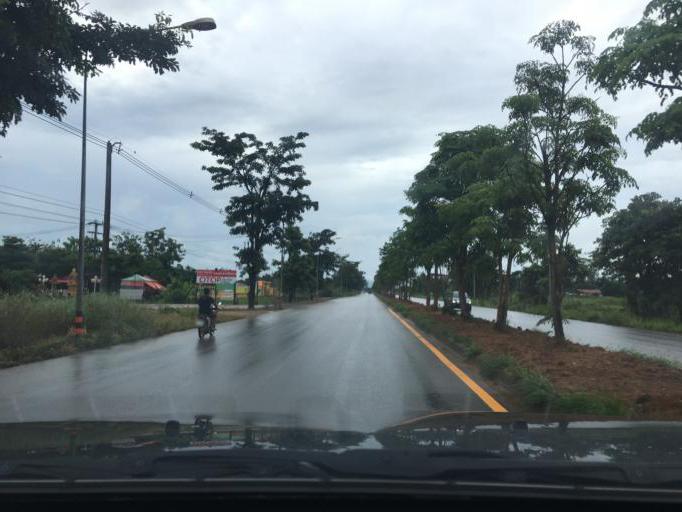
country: TH
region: Chiang Rai
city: Chiang Rai
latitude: 19.9567
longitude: 99.8660
